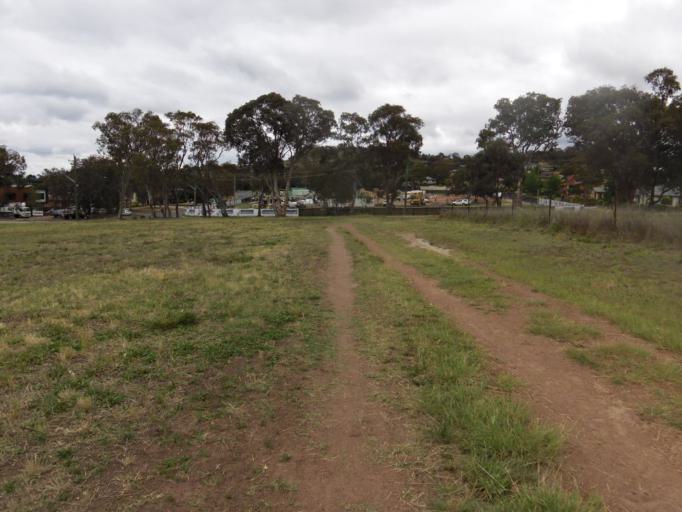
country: AU
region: Australian Capital Territory
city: Macquarie
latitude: -35.3461
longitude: 149.0280
